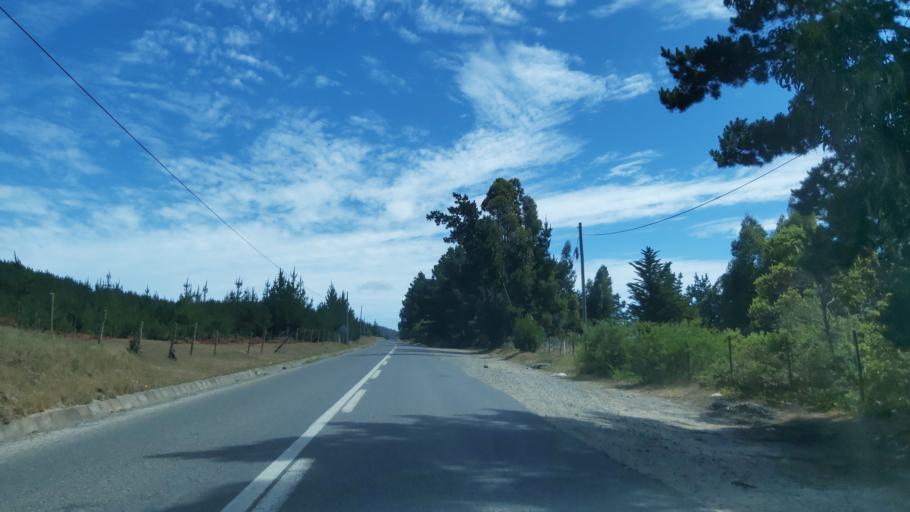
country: CL
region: Maule
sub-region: Provincia de Talca
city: Constitucion
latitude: -35.5542
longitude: -72.5815
